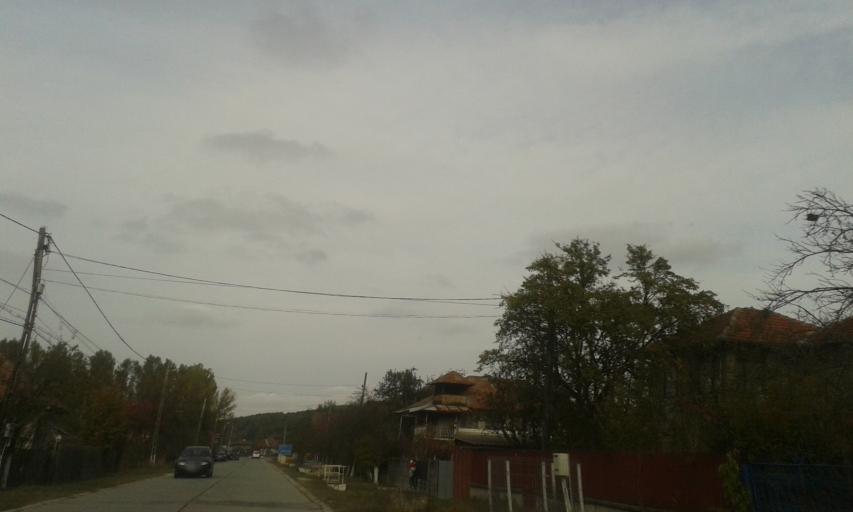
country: RO
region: Gorj
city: Logresti
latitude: 44.8851
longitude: 23.7131
